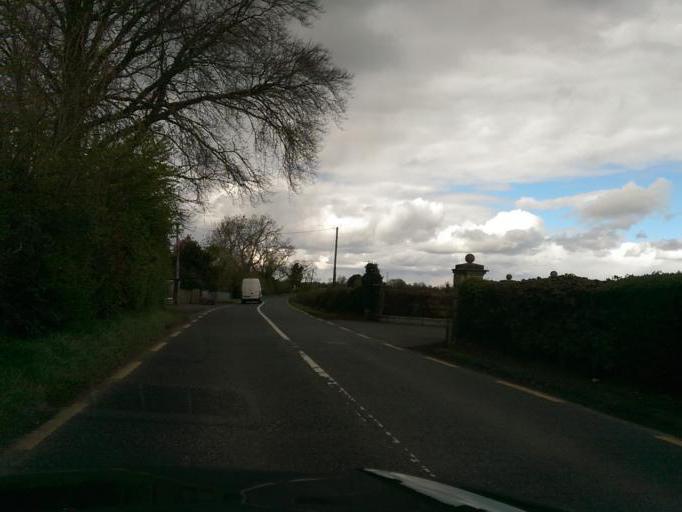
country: IE
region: Leinster
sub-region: An Mhi
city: Dunboyne
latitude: 53.3808
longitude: -6.4552
